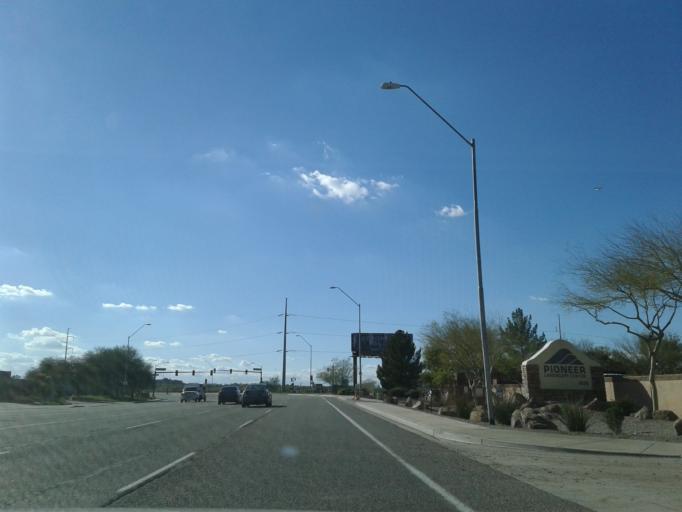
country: US
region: Arizona
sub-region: Maricopa County
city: Cave Creek
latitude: 33.6880
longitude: -112.0463
